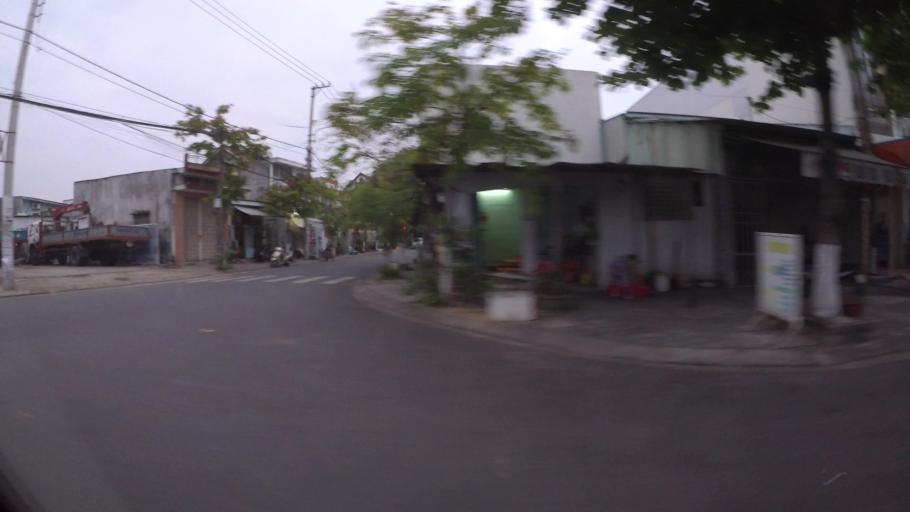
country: VN
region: Da Nang
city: Thanh Khe
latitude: 16.0558
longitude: 108.1747
